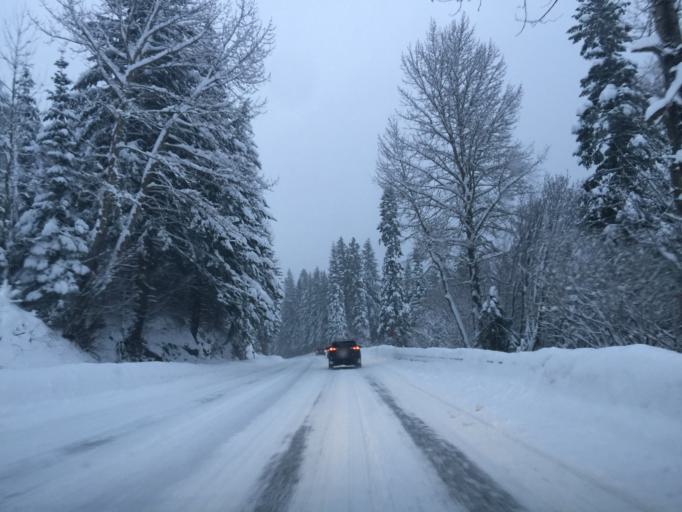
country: US
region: Washington
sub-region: Chelan County
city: Leavenworth
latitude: 47.7817
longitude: -120.9205
